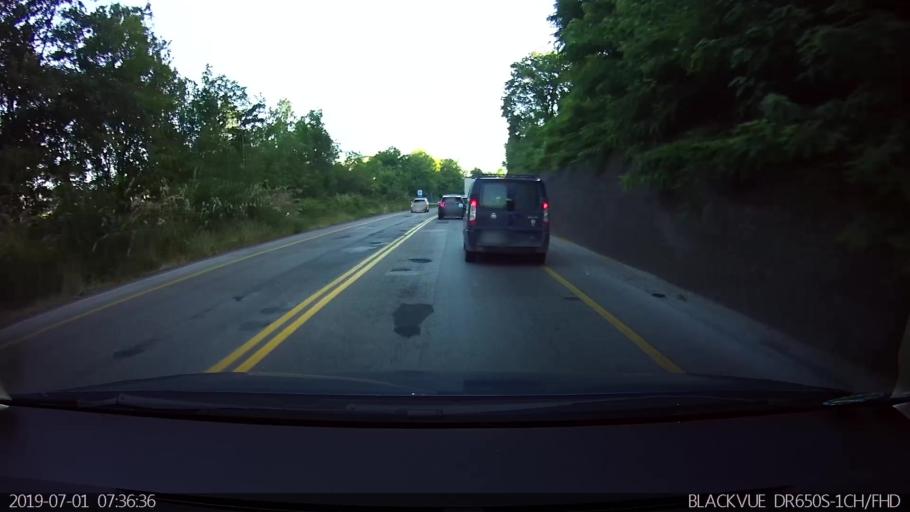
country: IT
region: Latium
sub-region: Provincia di Frosinone
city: Giuliano di Roma
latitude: 41.5326
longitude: 13.2667
